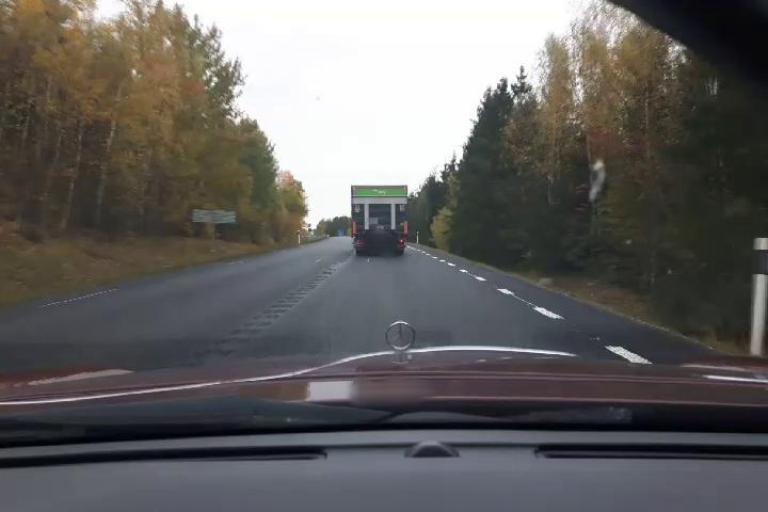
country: SE
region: Soedermanland
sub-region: Strangnas Kommun
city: Strangnas
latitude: 59.4056
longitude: 17.0201
